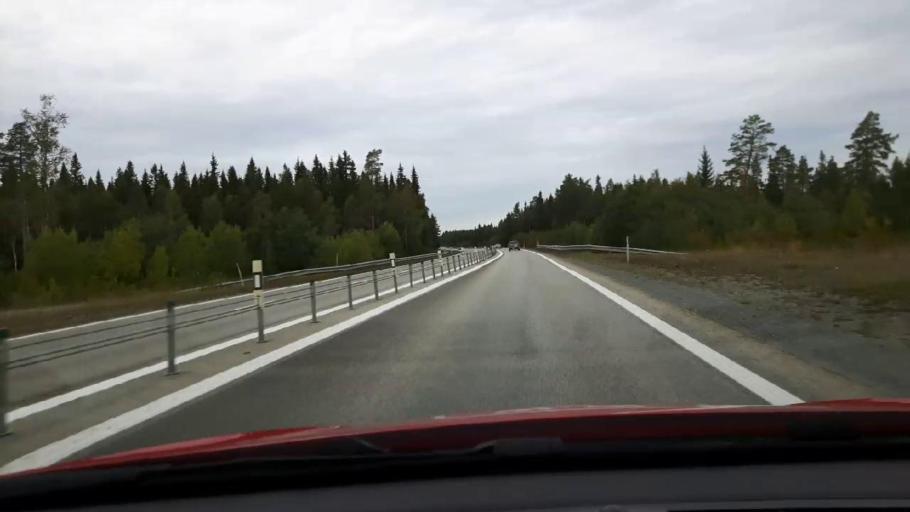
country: SE
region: Jaemtland
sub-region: OEstersunds Kommun
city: Brunflo
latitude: 63.1413
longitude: 14.7842
